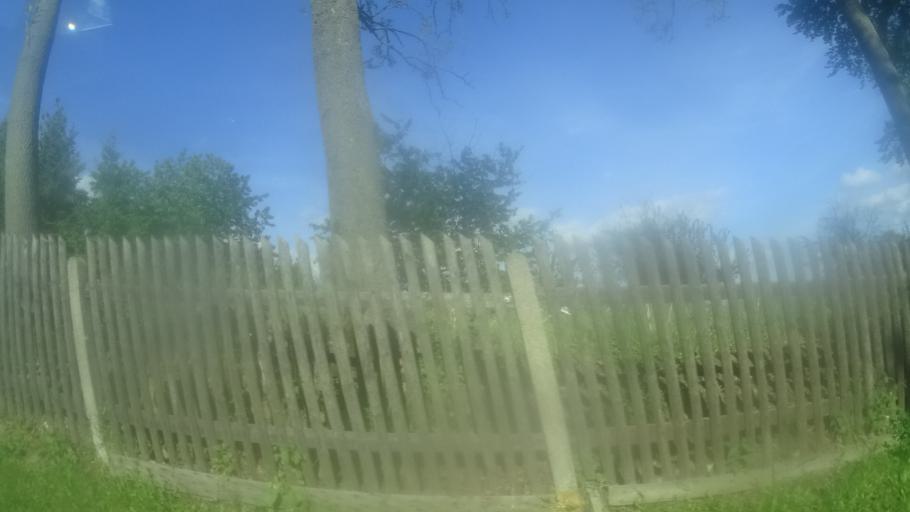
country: DE
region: Thuringia
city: Oberhain
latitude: 50.6297
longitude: 11.1233
